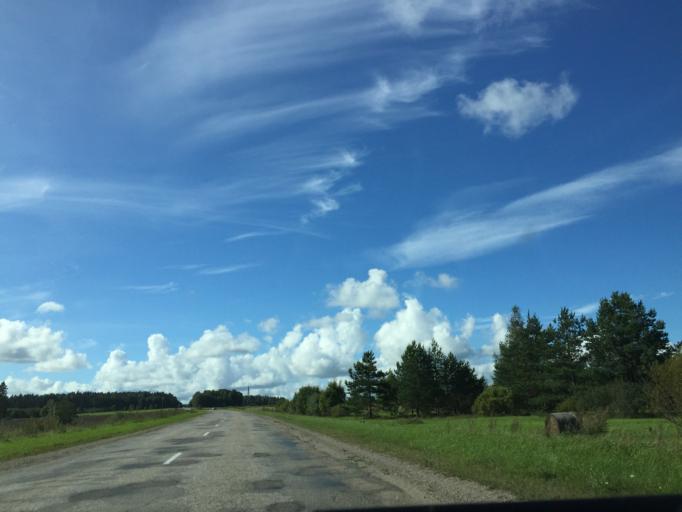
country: LV
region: Kuldigas Rajons
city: Kuldiga
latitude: 56.9866
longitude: 21.7977
